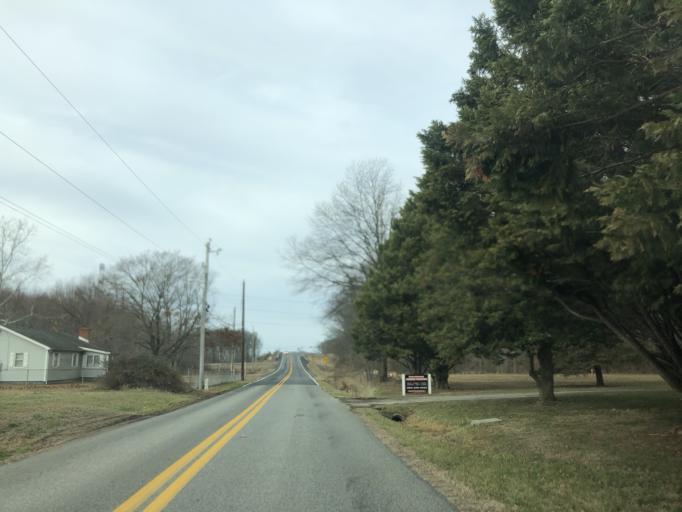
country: US
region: Delaware
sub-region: New Castle County
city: Middletown
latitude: 39.4140
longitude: -75.7624
